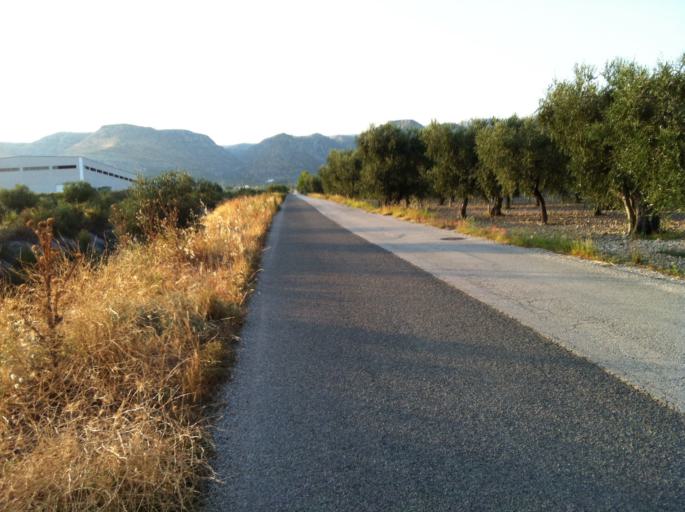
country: IT
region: Apulia
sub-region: Provincia di Foggia
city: Manfredonia
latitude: 41.6530
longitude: 15.9530
